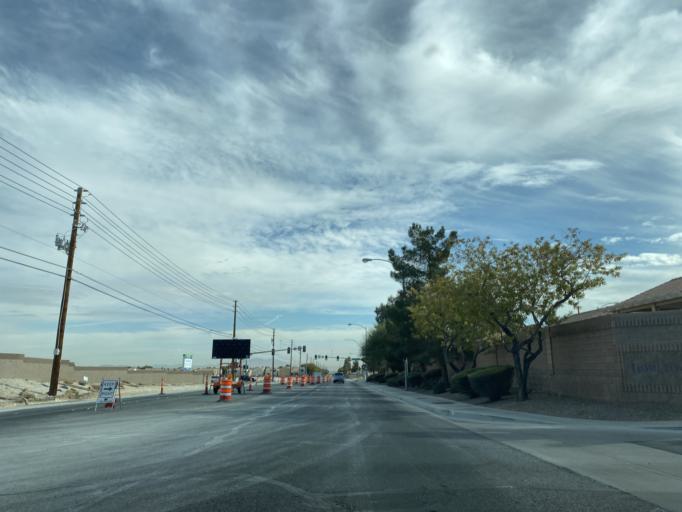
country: US
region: Nevada
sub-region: Clark County
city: North Las Vegas
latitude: 36.2468
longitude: -115.1817
